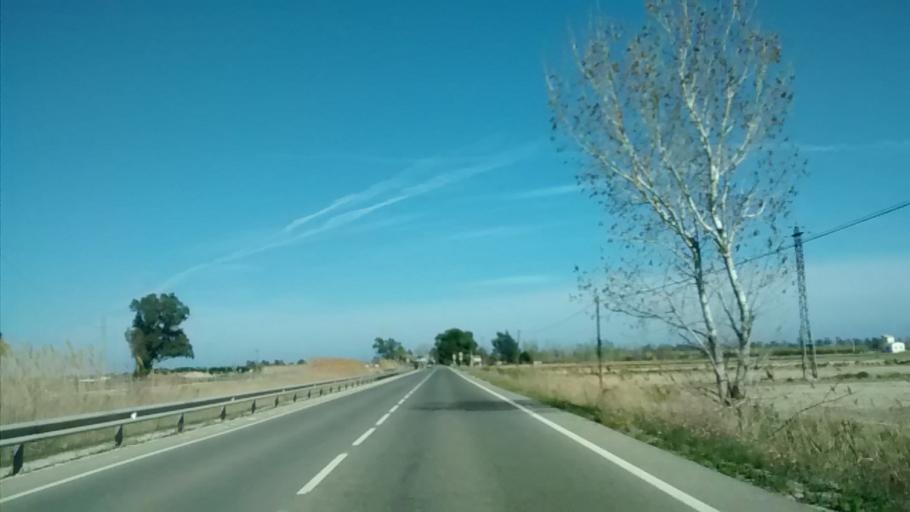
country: ES
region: Catalonia
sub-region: Provincia de Tarragona
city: Deltebre
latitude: 40.7064
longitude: 0.8067
